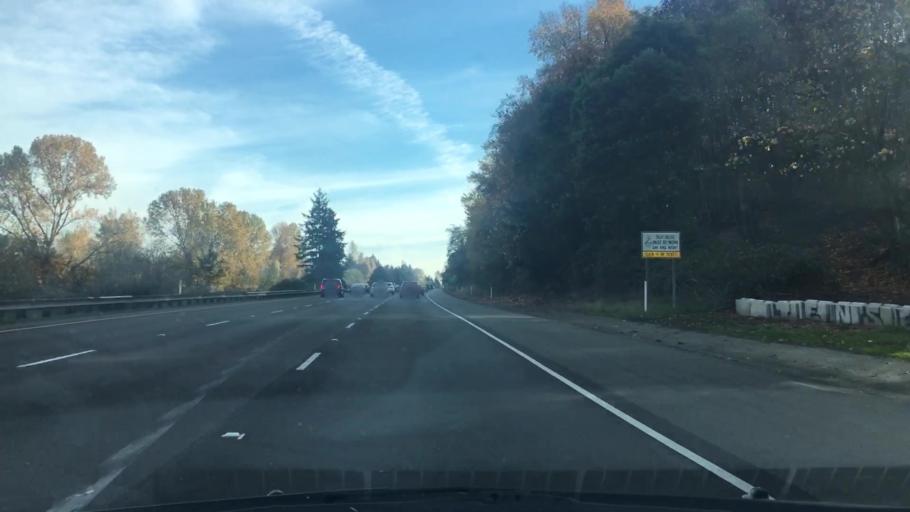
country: US
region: Washington
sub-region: King County
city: White Center
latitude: 47.5145
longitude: -122.3291
